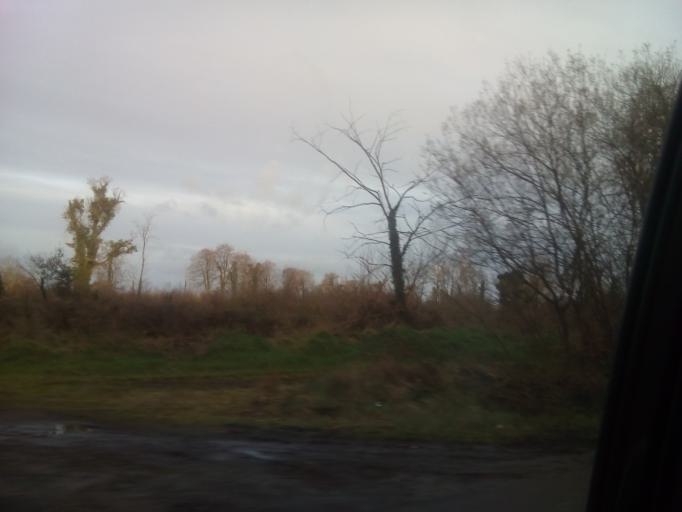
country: IE
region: Leinster
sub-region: Laois
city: Abbeyleix
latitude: 52.8815
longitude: -7.3640
